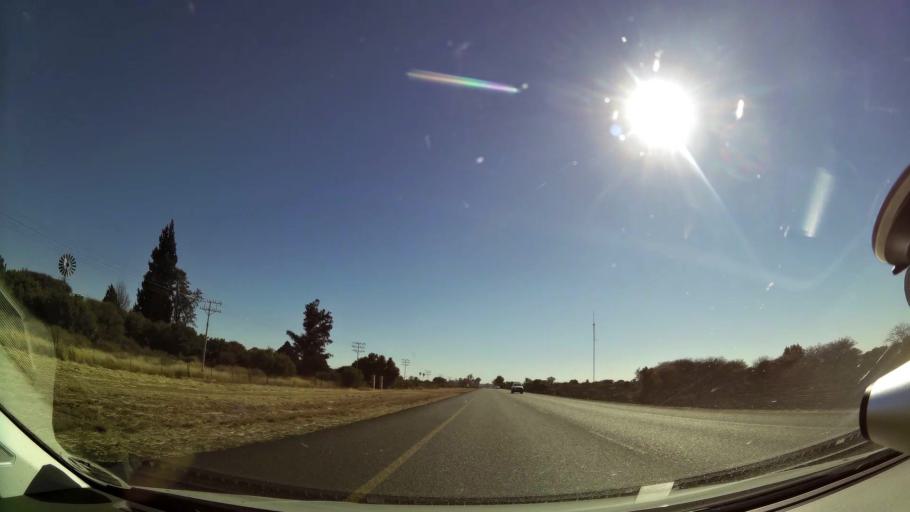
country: ZA
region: Northern Cape
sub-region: Frances Baard District Municipality
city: Warrenton
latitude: -28.1343
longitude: 24.8417
